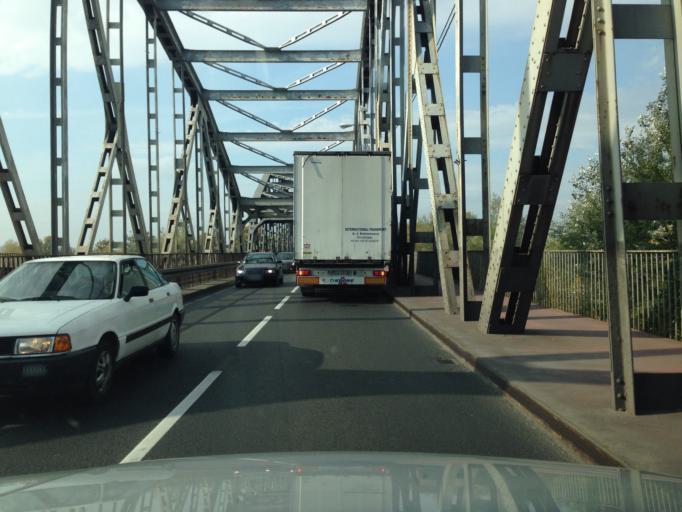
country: PL
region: Kujawsko-Pomorskie
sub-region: Grudziadz
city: Grudziadz
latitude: 53.4858
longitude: 18.7329
